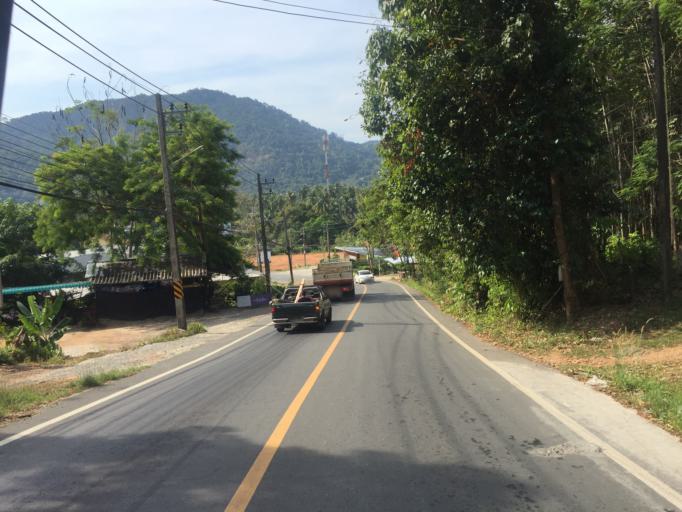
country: TH
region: Trat
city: Laem Ngop
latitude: 12.1367
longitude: 102.2763
